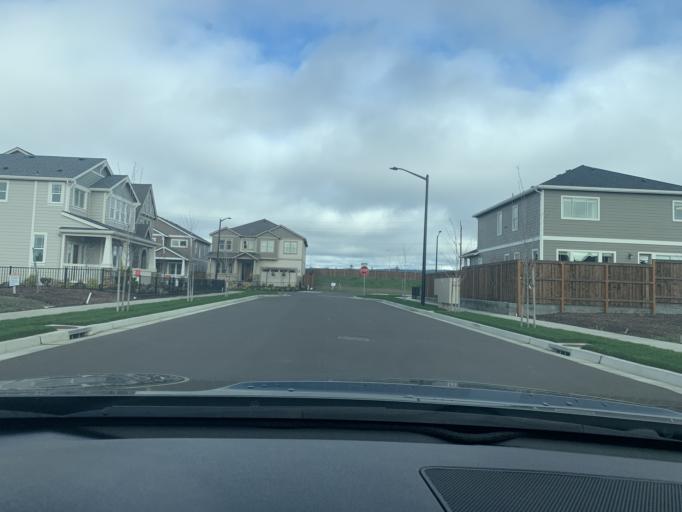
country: US
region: Oregon
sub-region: Washington County
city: North Plains
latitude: 45.5951
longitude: -122.9764
